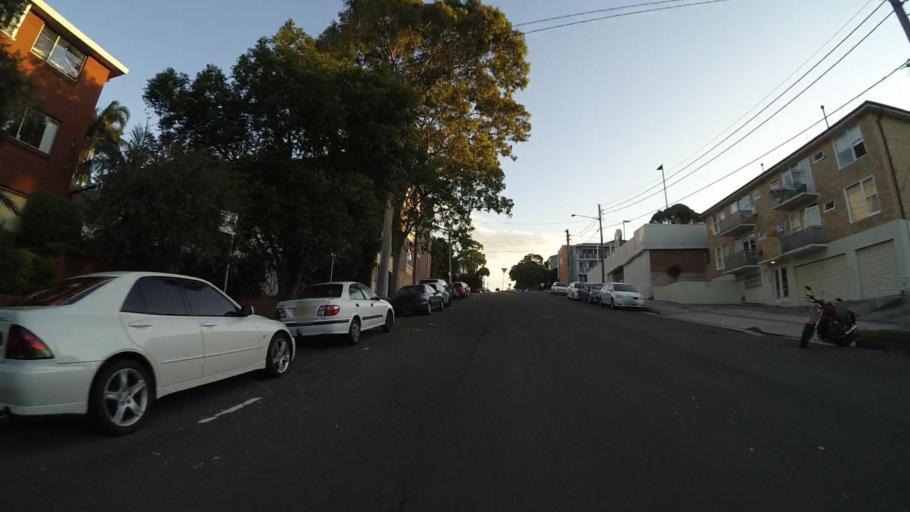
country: AU
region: New South Wales
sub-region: Randwick
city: Coogee
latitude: -33.9196
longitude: 151.2522
